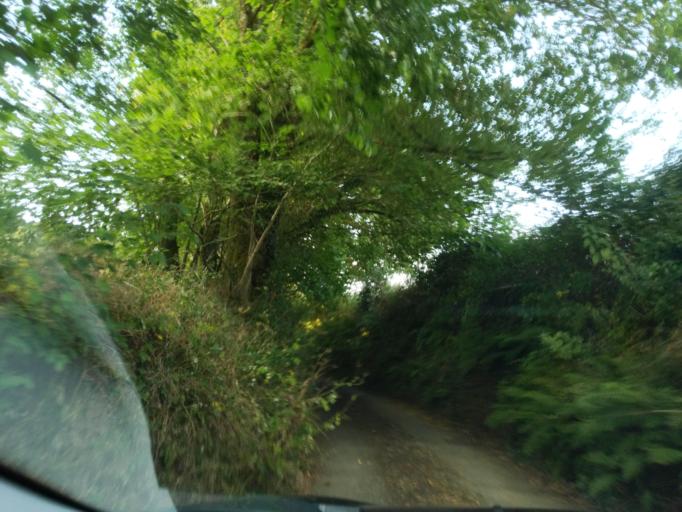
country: GB
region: England
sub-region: Cornwall
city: Fowey
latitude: 50.3646
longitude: -4.5949
